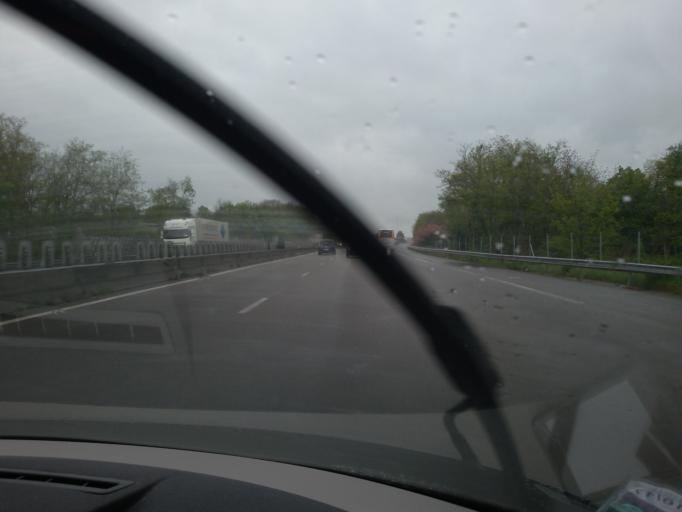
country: FR
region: Rhone-Alpes
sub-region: Departement de l'Isere
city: Roussillon
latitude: 45.3855
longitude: 4.8058
